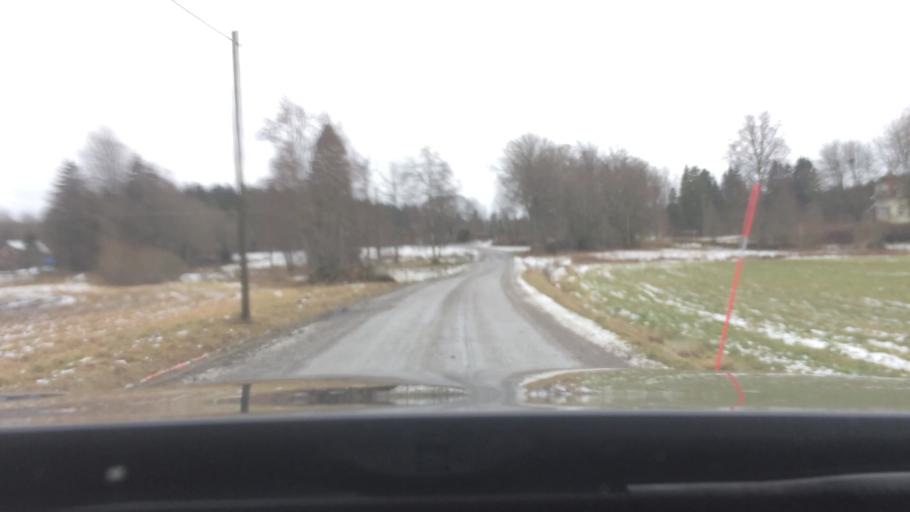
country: SE
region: Vaestra Goetaland
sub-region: Falkopings Kommun
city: Floby
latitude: 57.9912
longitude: 13.4050
